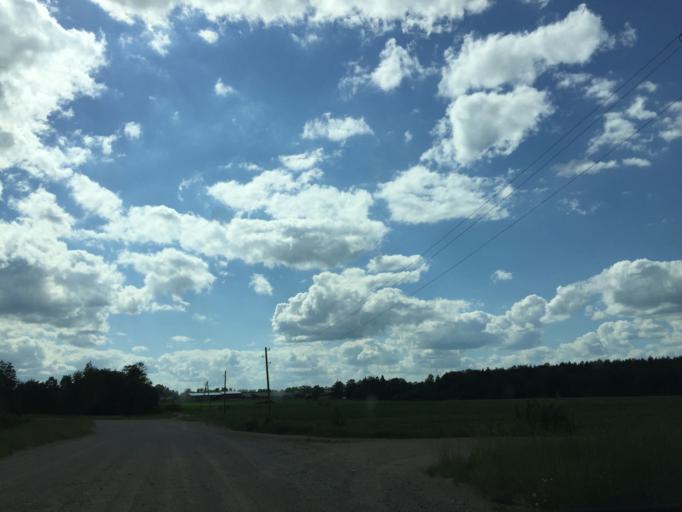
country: LV
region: Tukuma Rajons
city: Tukums
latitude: 56.9082
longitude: 23.1611
